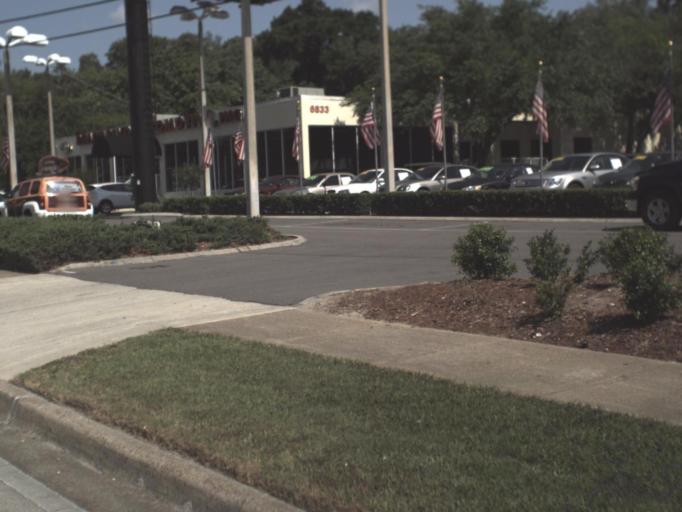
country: US
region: Florida
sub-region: Duval County
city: Jacksonville
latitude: 30.2898
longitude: -81.5882
